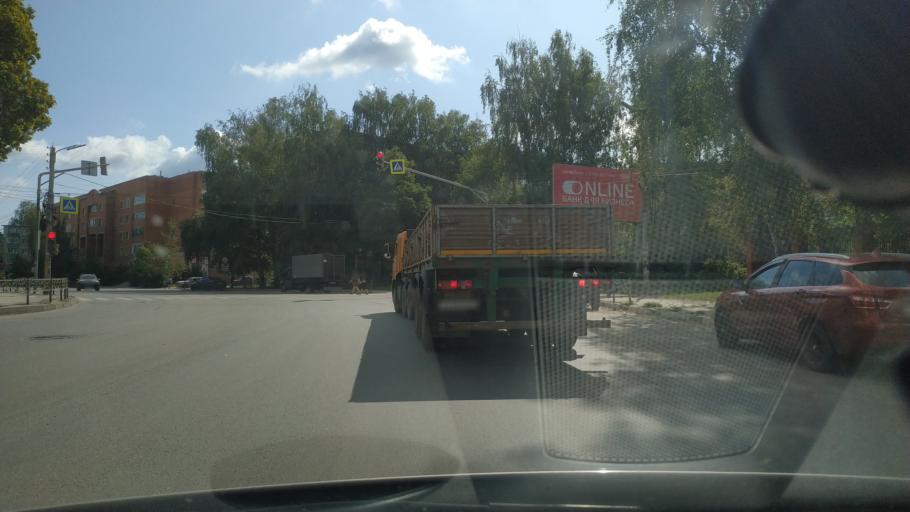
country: RU
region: Rjazan
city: Ryazan'
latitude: 54.6060
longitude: 39.7048
